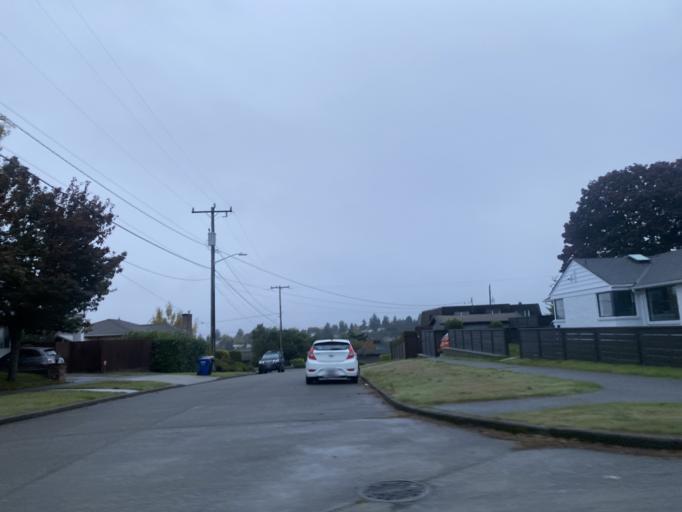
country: US
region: Washington
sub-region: King County
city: Seattle
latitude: 47.6505
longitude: -122.4058
